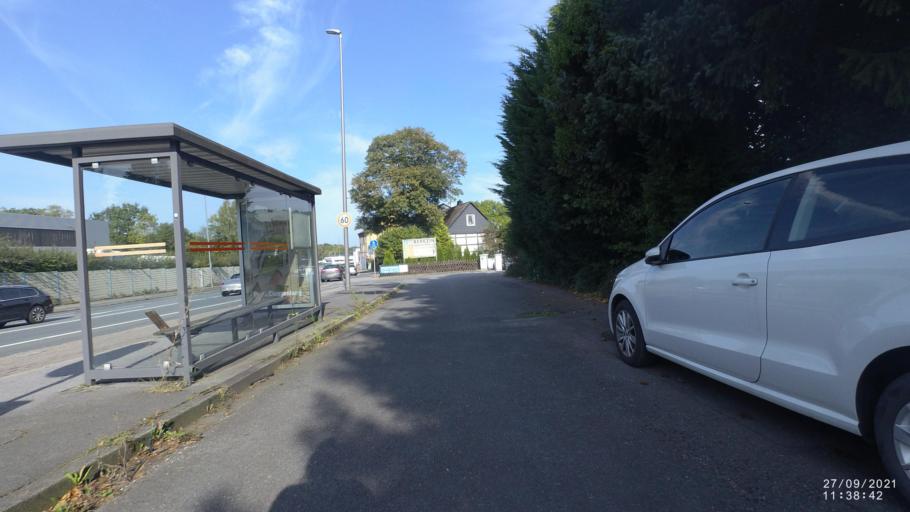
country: DE
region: North Rhine-Westphalia
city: Iserlohn
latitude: 51.4027
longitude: 7.6989
